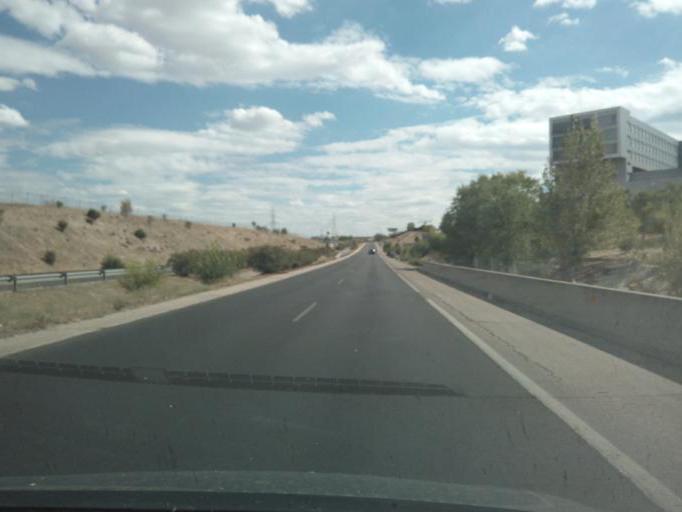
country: ES
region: Madrid
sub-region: Provincia de Madrid
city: San Sebastian de los Reyes
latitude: 40.5595
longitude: -3.6086
